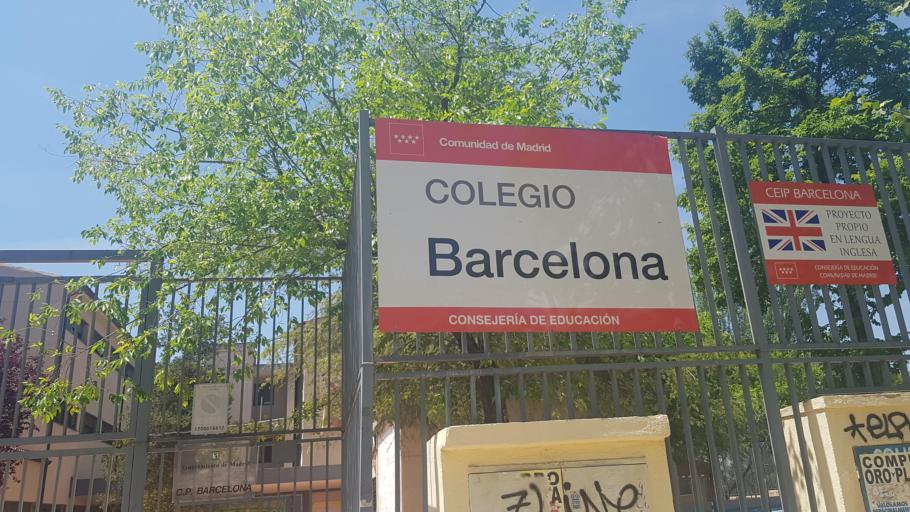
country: ES
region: Madrid
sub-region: Provincia de Madrid
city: Villaverde
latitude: 40.3587
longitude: -3.6962
